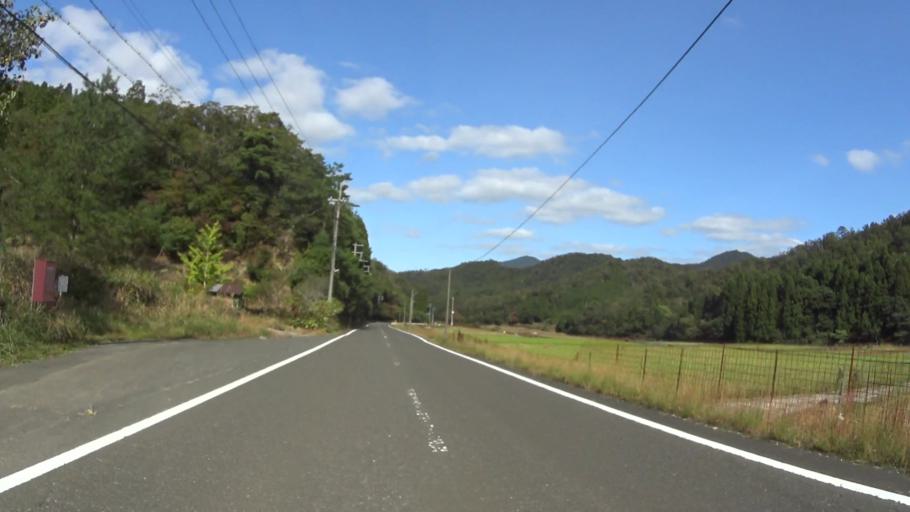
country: JP
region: Hyogo
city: Toyooka
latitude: 35.5538
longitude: 134.9774
